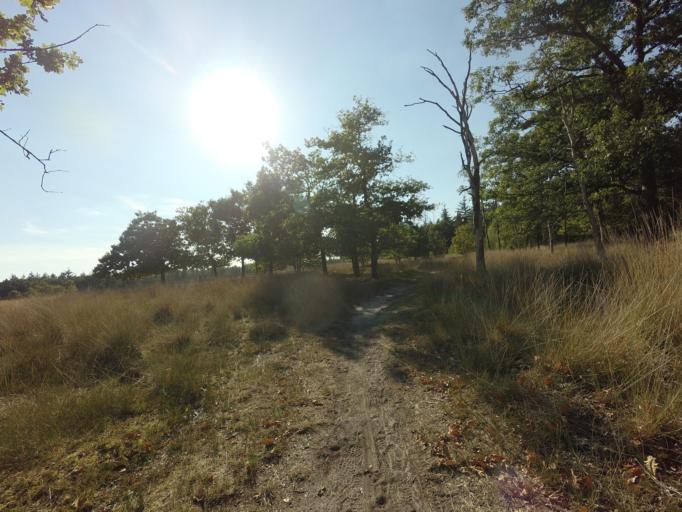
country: NL
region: North Brabant
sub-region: Gemeente Someren
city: Someren
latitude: 51.3726
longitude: 5.6582
